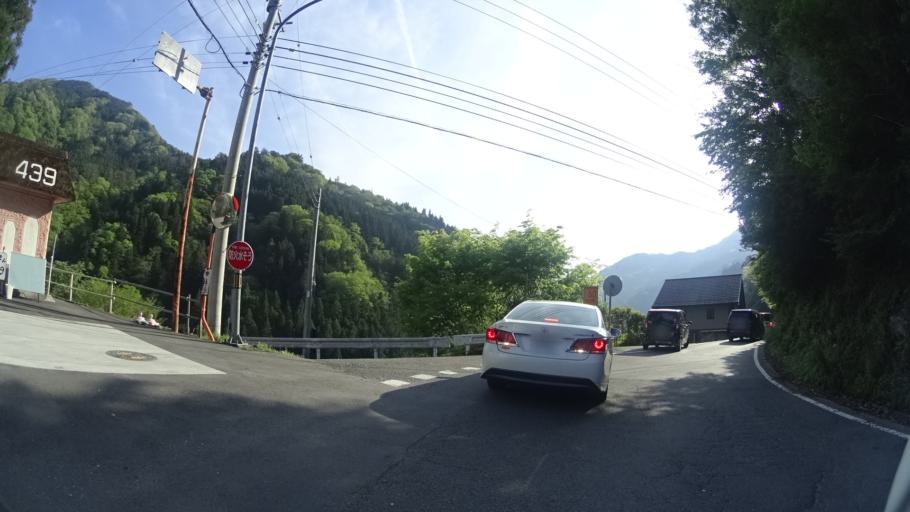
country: JP
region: Tokushima
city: Ikedacho
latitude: 33.8714
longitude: 133.9154
